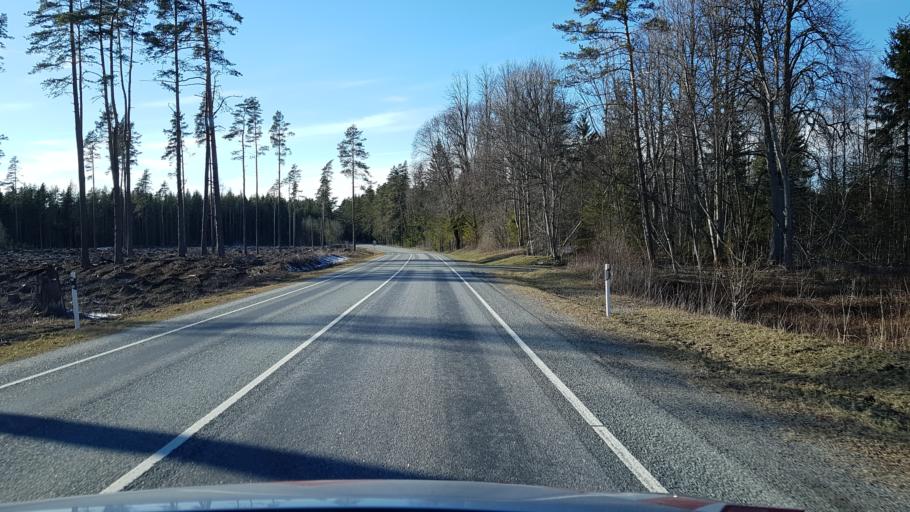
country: EE
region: Laeaene-Virumaa
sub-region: Tapa vald
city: Tapa
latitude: 59.4249
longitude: 25.9869
